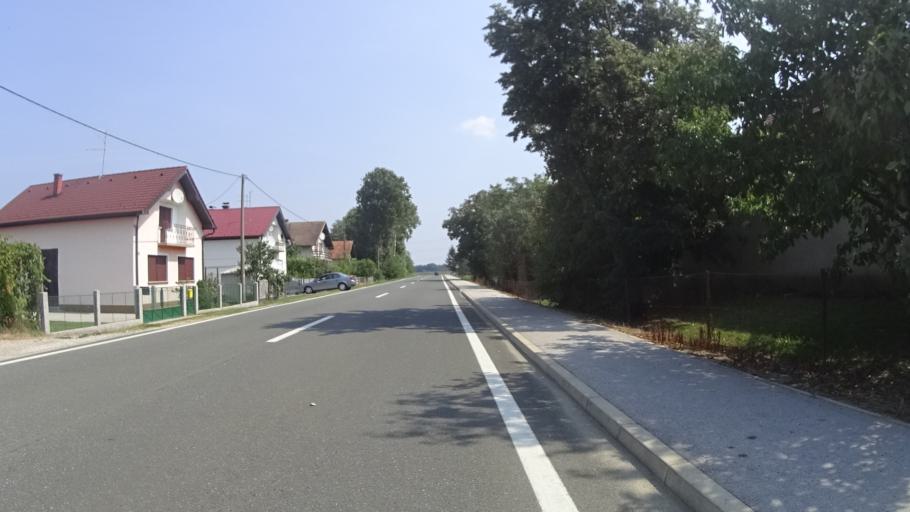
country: HR
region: Medimurska
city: Hodosan
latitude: 46.3969
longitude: 16.6454
